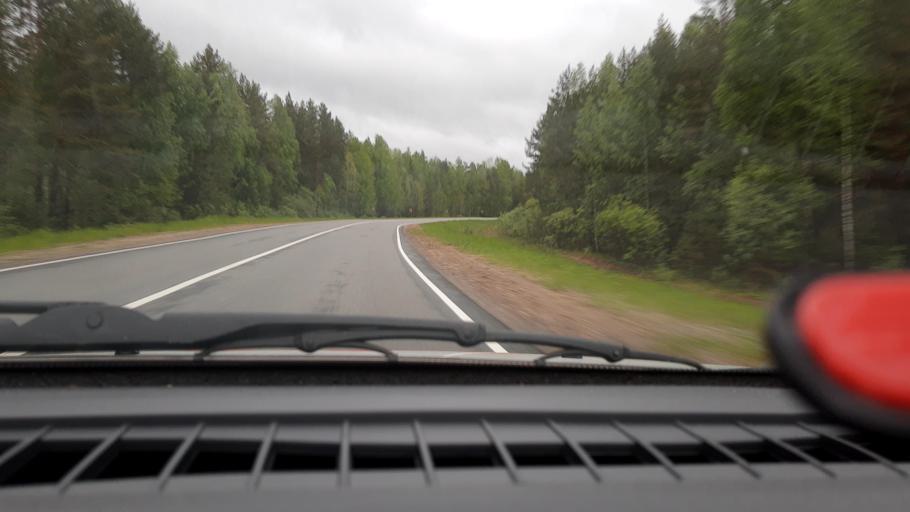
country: RU
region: Nizjnij Novgorod
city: Krasnyye Baki
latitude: 57.2110
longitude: 45.4622
